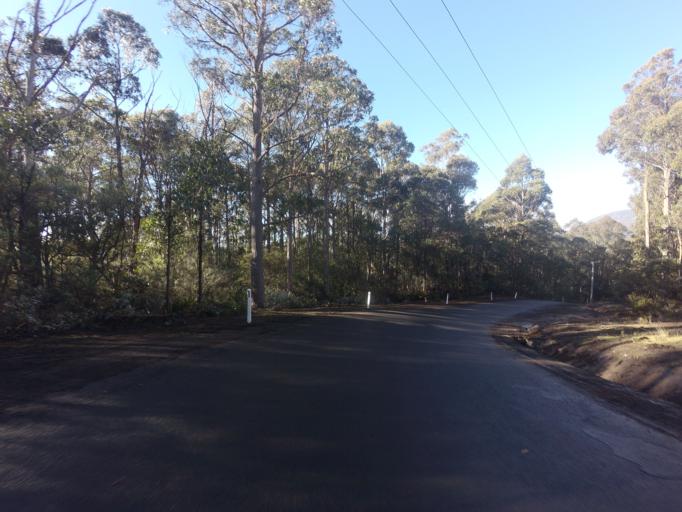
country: AU
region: Tasmania
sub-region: Glenorchy
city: Berriedale
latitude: -42.8374
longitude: 147.1602
